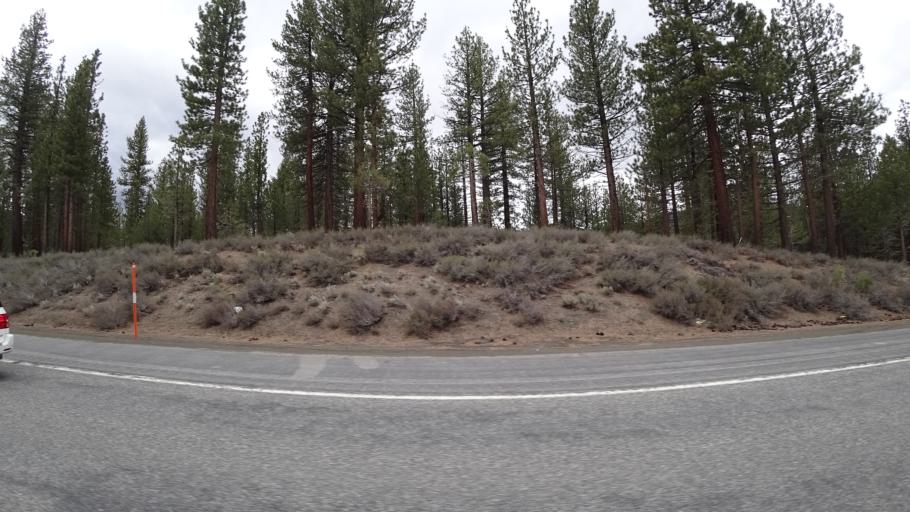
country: US
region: California
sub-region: Mono County
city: Mammoth Lakes
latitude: 37.7771
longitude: -119.0179
